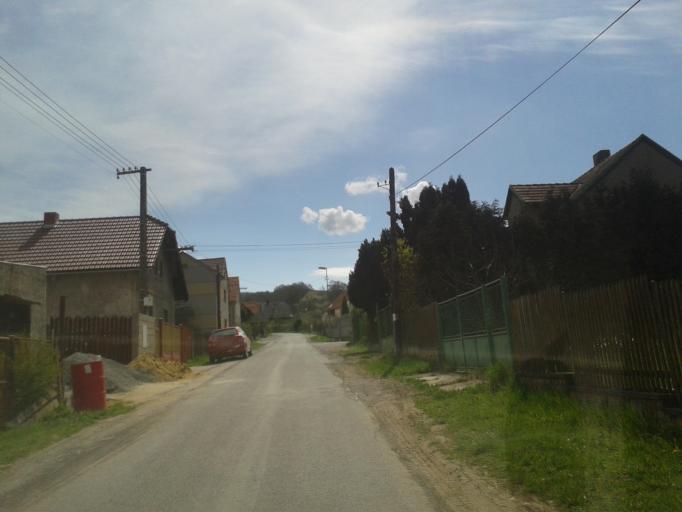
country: CZ
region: Central Bohemia
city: Dobris
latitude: 49.8696
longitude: 14.1411
